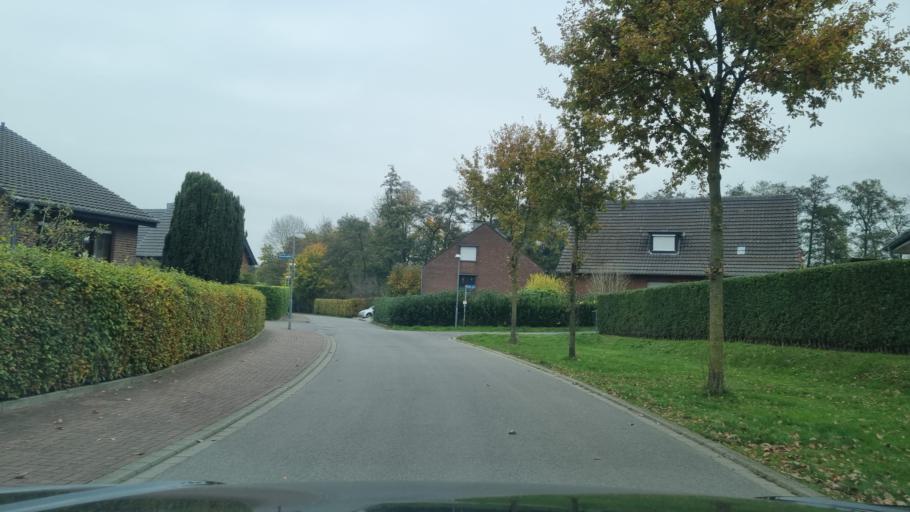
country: DE
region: North Rhine-Westphalia
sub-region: Regierungsbezirk Dusseldorf
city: Kranenburg
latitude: 51.7870
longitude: 6.0695
